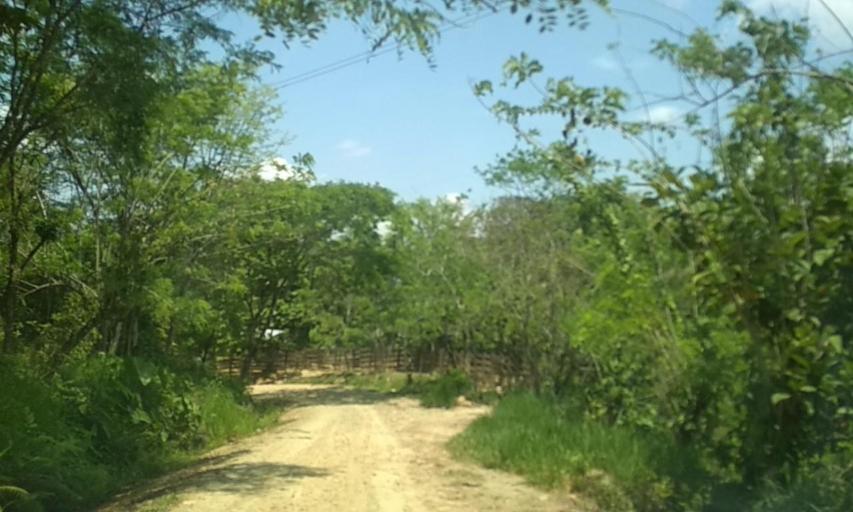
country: MX
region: Chiapas
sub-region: Tecpatan
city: Raudales Malpaso
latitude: 17.3943
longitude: -93.7260
